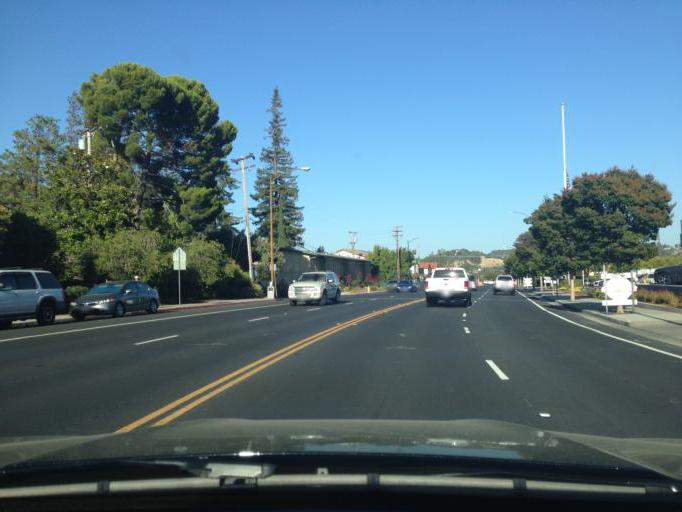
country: US
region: California
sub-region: Santa Clara County
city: Los Gatos
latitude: 37.2361
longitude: -121.9666
